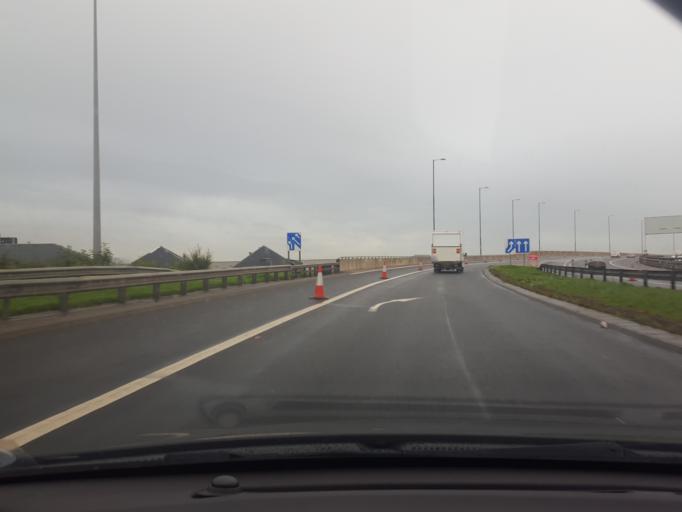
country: GB
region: Scotland
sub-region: Glasgow City
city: Glasgow
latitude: 55.8510
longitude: -4.2672
